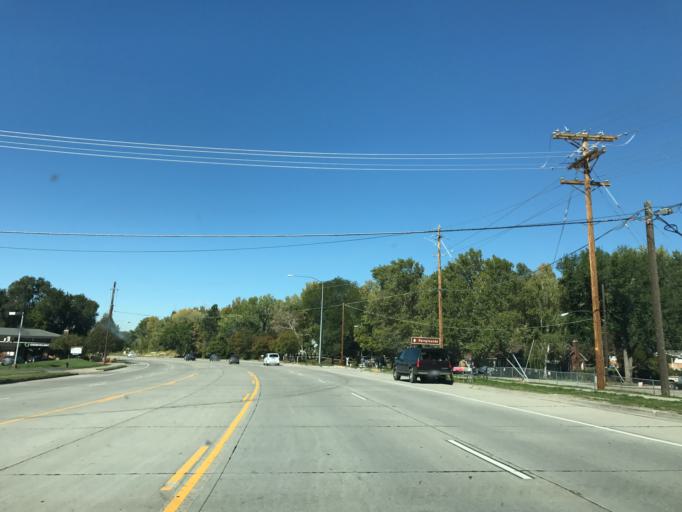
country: US
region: Utah
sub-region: Weber County
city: Ogden
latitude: 41.2434
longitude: -111.9479
